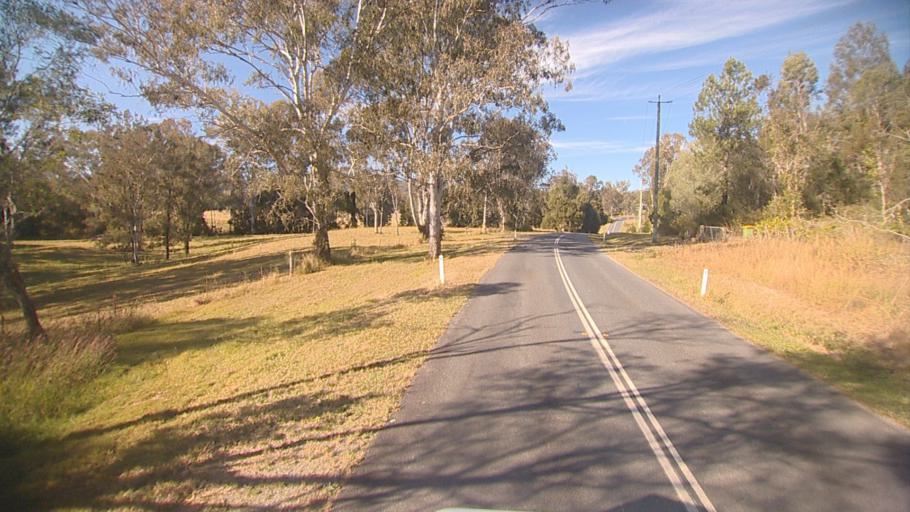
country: AU
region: Queensland
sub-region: Logan
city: Windaroo
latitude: -27.8064
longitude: 153.1701
